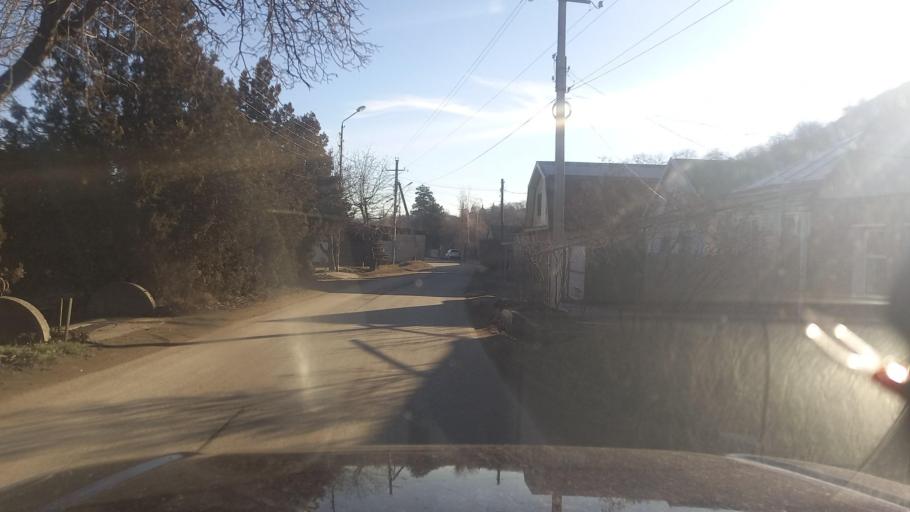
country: RU
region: Stavropol'skiy
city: Svobody
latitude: 44.0237
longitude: 43.0621
